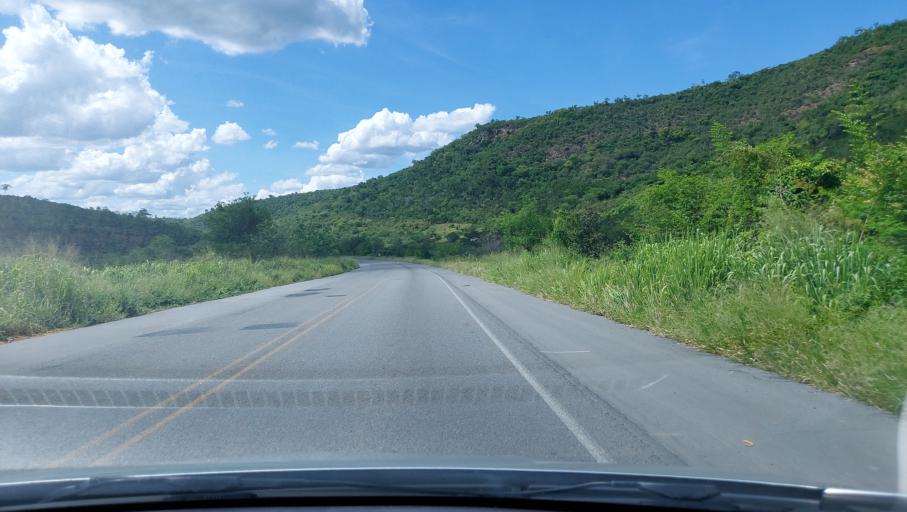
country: BR
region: Bahia
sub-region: Itaberaba
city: Itaberaba
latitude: -12.4975
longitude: -40.5022
